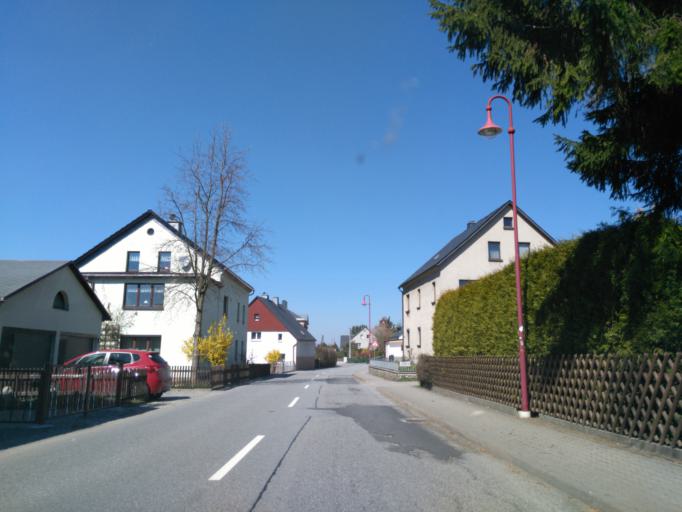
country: DE
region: Saxony
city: Crottendorf
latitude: 50.5037
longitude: 12.9368
